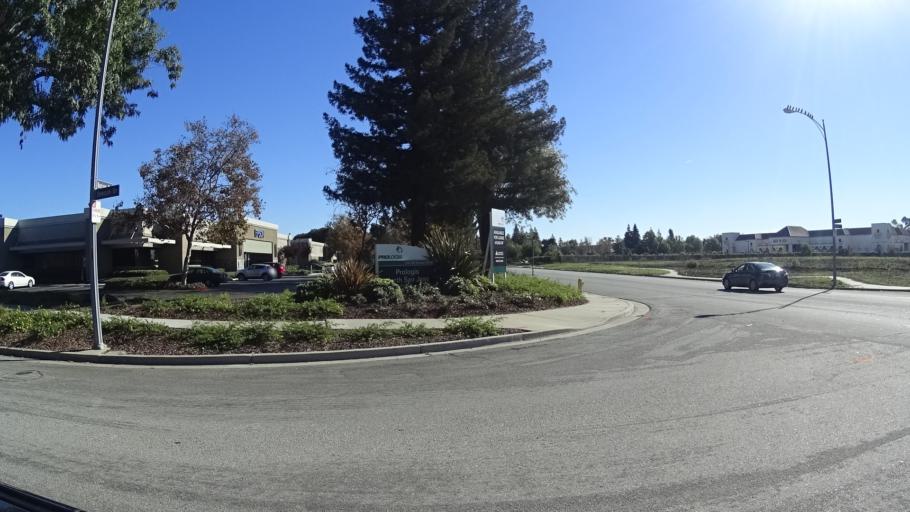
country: US
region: California
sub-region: Santa Clara County
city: San Jose
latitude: 37.3743
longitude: -121.9137
